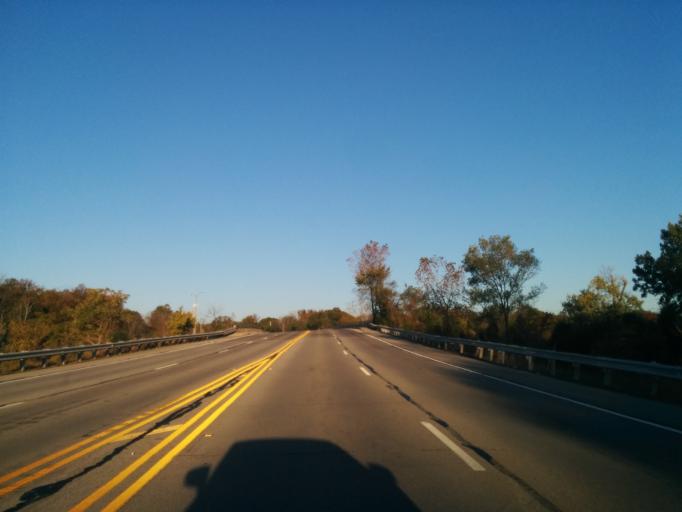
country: US
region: Illinois
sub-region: DuPage County
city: Lombard
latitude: 41.8885
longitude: -88.0356
